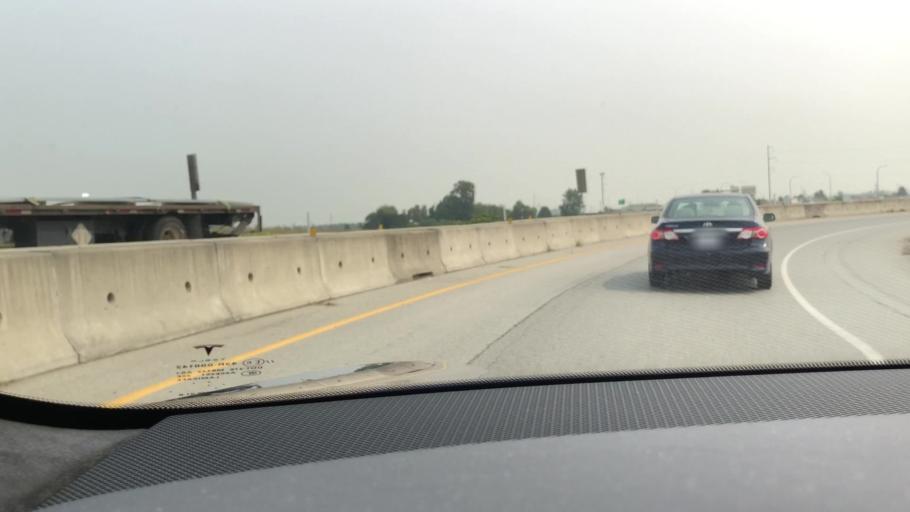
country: CA
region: British Columbia
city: Ladner
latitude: 49.1078
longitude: -123.0540
